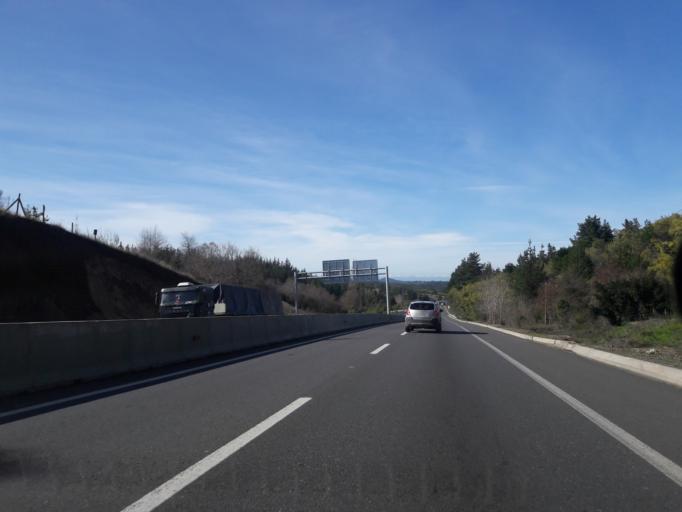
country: CL
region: Biobio
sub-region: Provincia de Biobio
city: Yumbel
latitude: -36.9640
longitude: -72.7050
